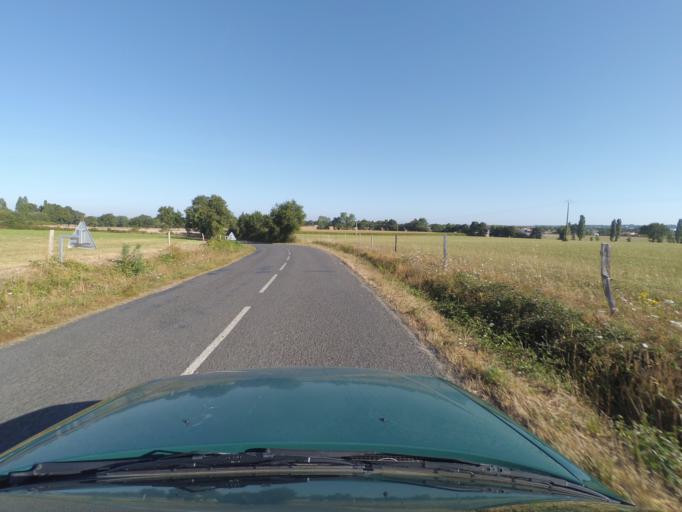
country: FR
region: Pays de la Loire
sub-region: Departement de la Loire-Atlantique
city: Le Bignon
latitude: 47.1018
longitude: -1.5028
